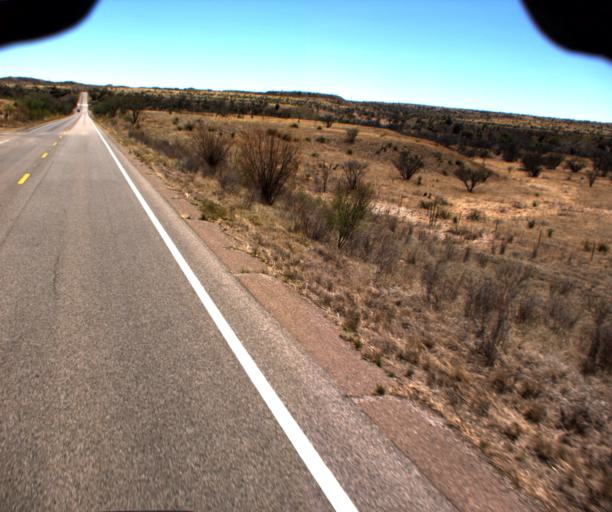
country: US
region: Arizona
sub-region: Pima County
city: Corona de Tucson
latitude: 31.7416
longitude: -110.6659
